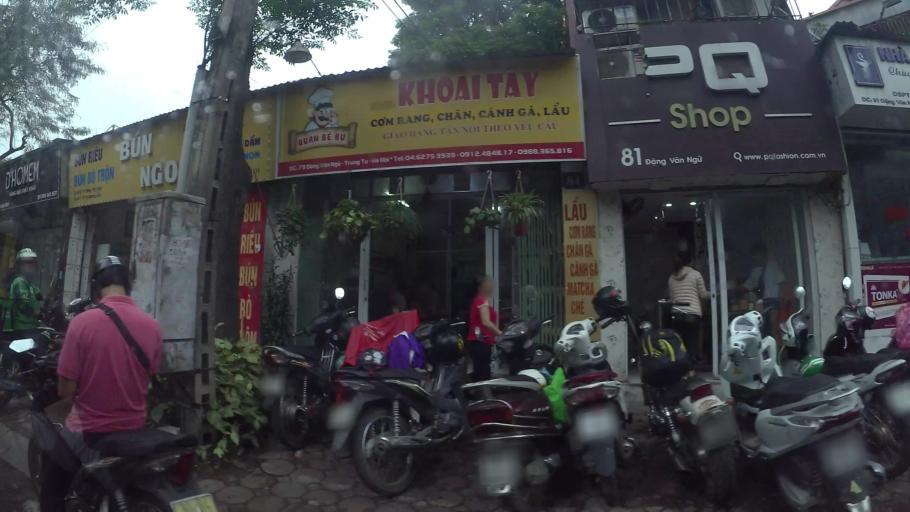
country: VN
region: Ha Noi
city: Dong Da
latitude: 21.0105
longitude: 105.8310
